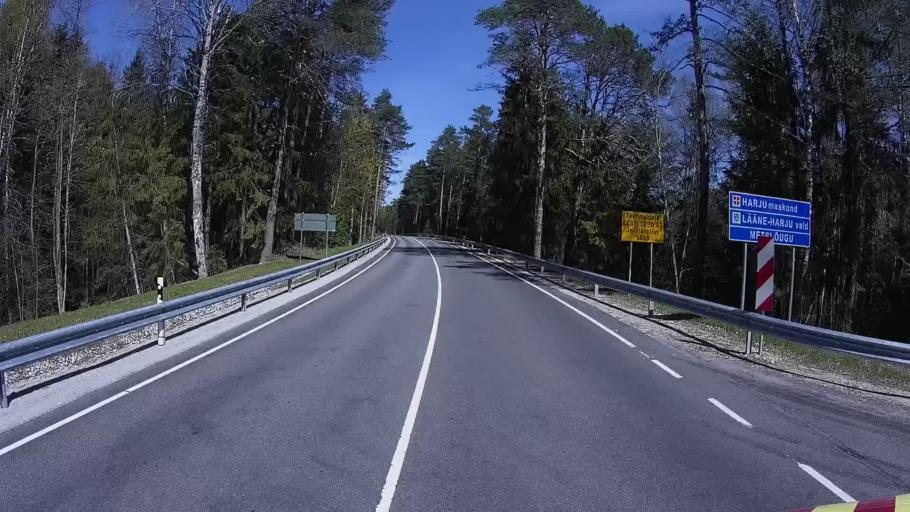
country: EE
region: Harju
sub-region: Nissi vald
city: Turba
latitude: 59.1303
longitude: 24.0716
